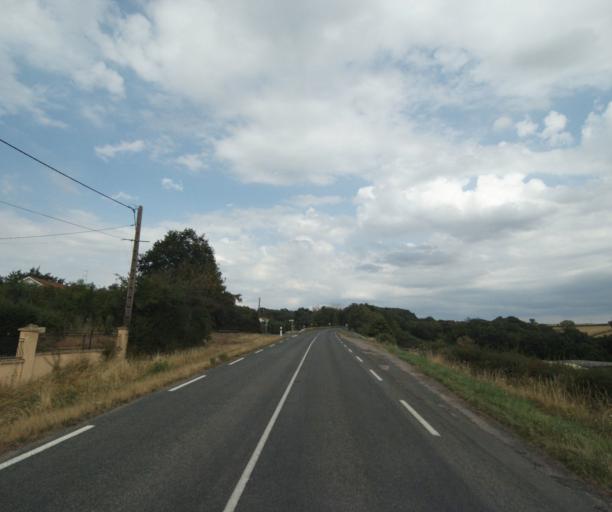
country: FR
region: Bourgogne
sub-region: Departement de Saone-et-Loire
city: Gueugnon
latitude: 46.6005
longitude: 4.1014
